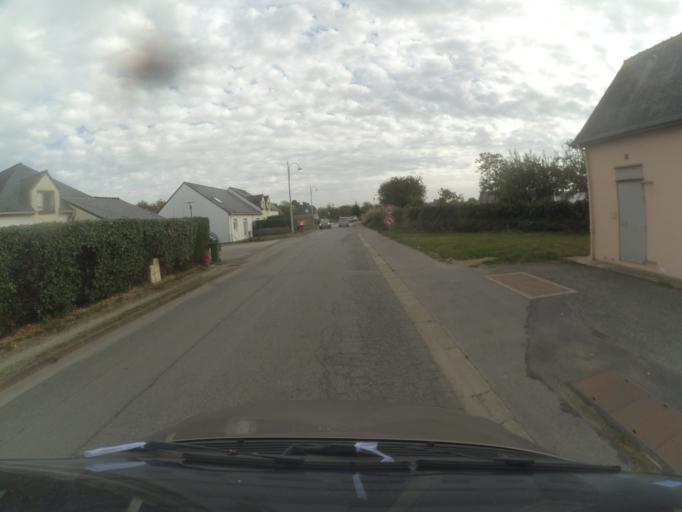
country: FR
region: Brittany
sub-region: Departement du Morbihan
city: Erdeven
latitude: 47.6423
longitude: -3.1535
